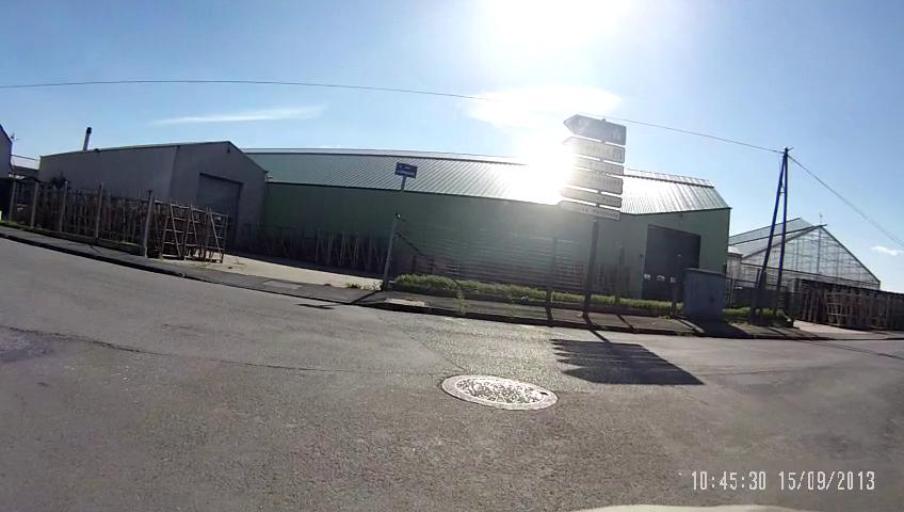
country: FR
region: Nord-Pas-de-Calais
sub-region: Departement du Nord
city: Teteghem
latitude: 51.0477
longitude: 2.4345
